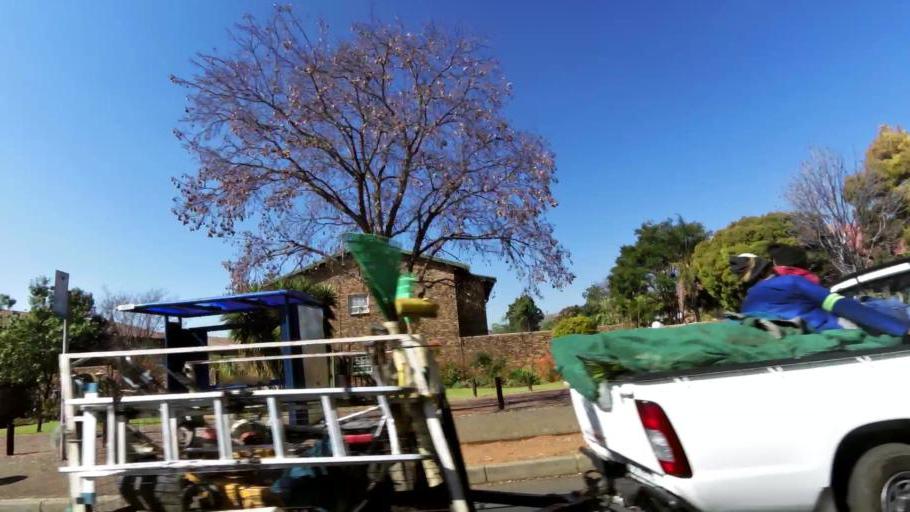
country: ZA
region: Gauteng
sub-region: City of Johannesburg Metropolitan Municipality
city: Roodepoort
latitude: -26.1271
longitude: 27.9470
